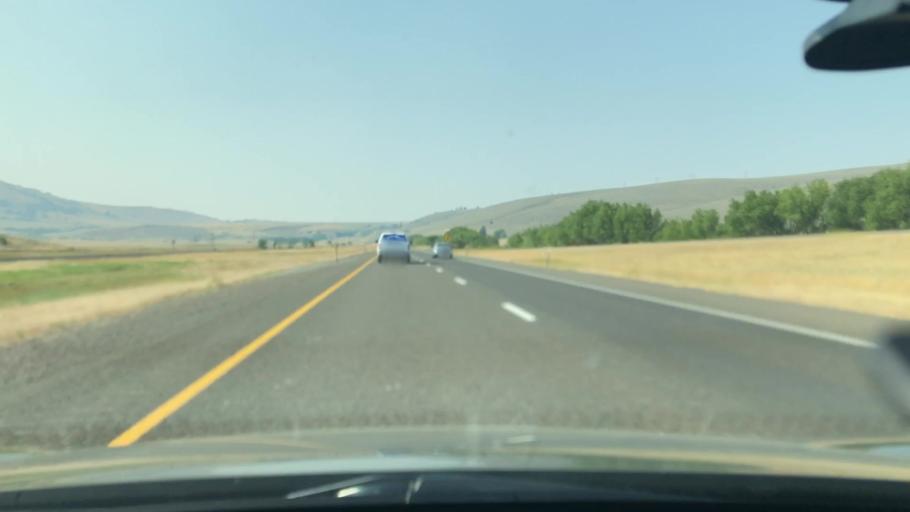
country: US
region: Oregon
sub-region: Union County
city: Union
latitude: 45.1242
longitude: -117.9626
